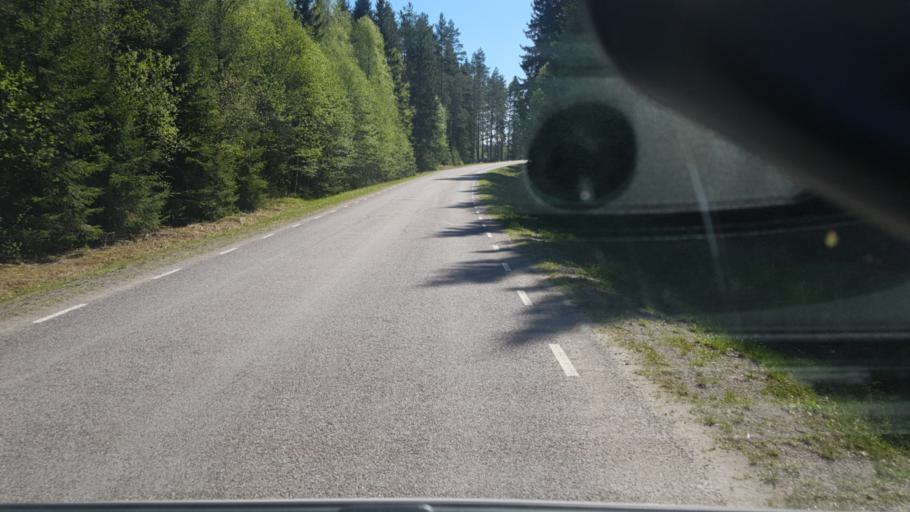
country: SE
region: Vaermland
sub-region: Eda Kommun
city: Charlottenberg
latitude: 59.9538
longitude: 12.3870
